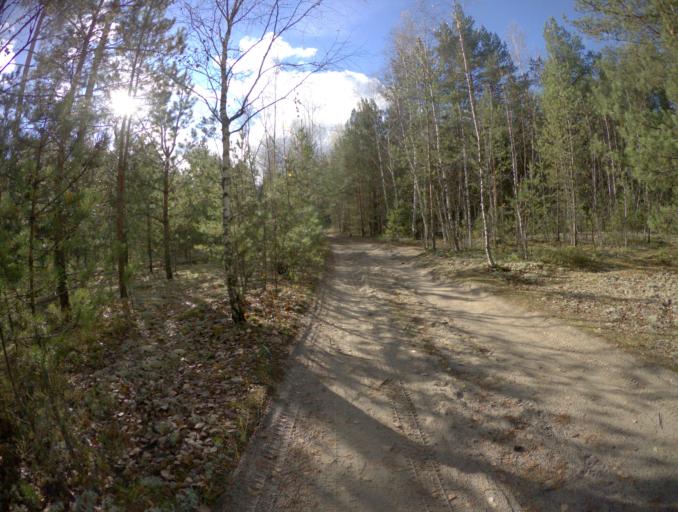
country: RU
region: Vladimir
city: Raduzhnyy
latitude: 56.0585
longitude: 40.3284
